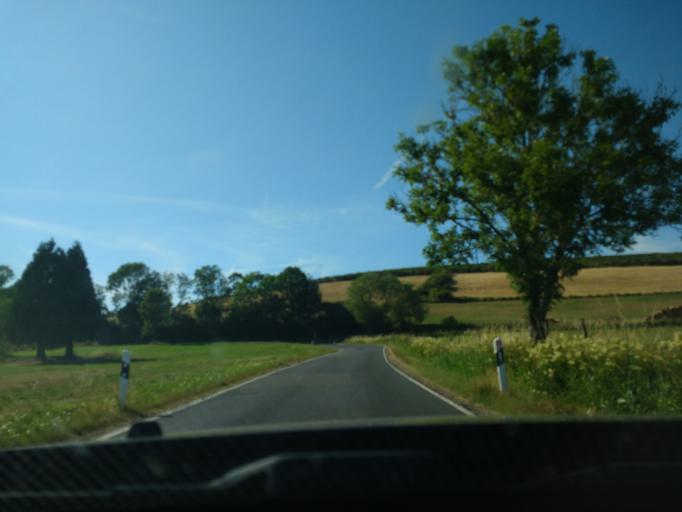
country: DE
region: Rheinland-Pfalz
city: Salm
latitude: 50.1501
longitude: 6.6975
